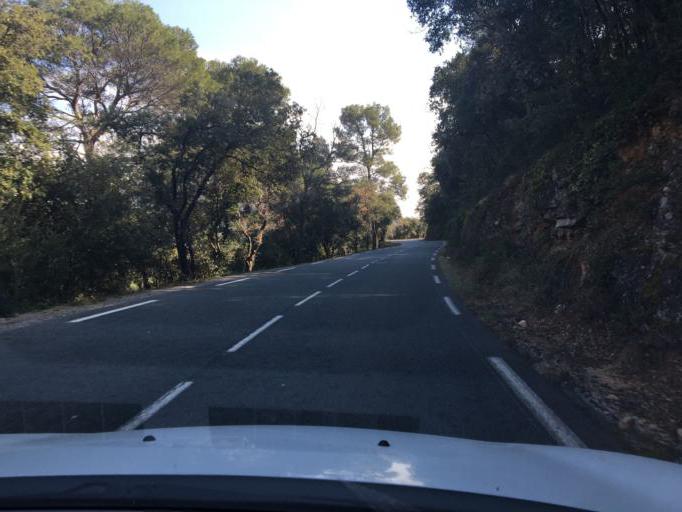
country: FR
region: Provence-Alpes-Cote d'Azur
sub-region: Departement du Var
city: Bargemon
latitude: 43.6120
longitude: 6.5489
